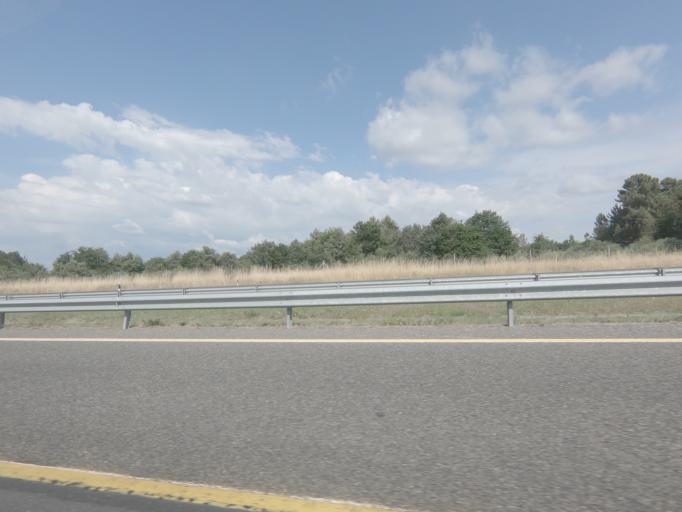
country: ES
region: Galicia
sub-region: Provincia de Ourense
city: Taboadela
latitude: 42.2588
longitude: -7.8687
